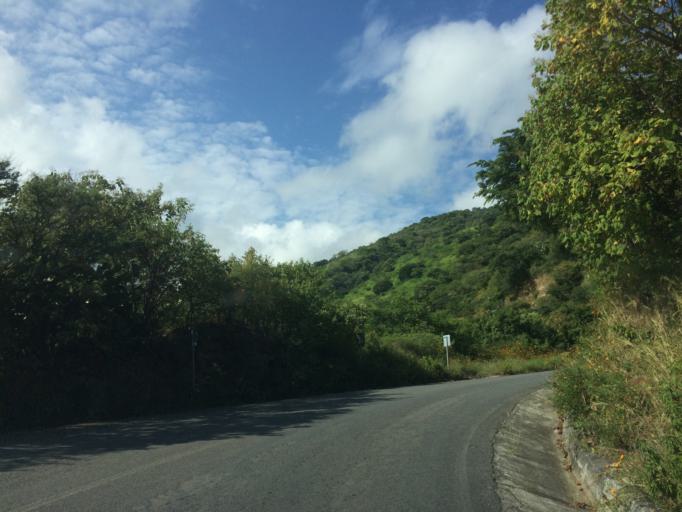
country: MX
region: Nayarit
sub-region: Ahuacatlan
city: Ahuacatlan
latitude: 21.0155
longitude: -104.4762
